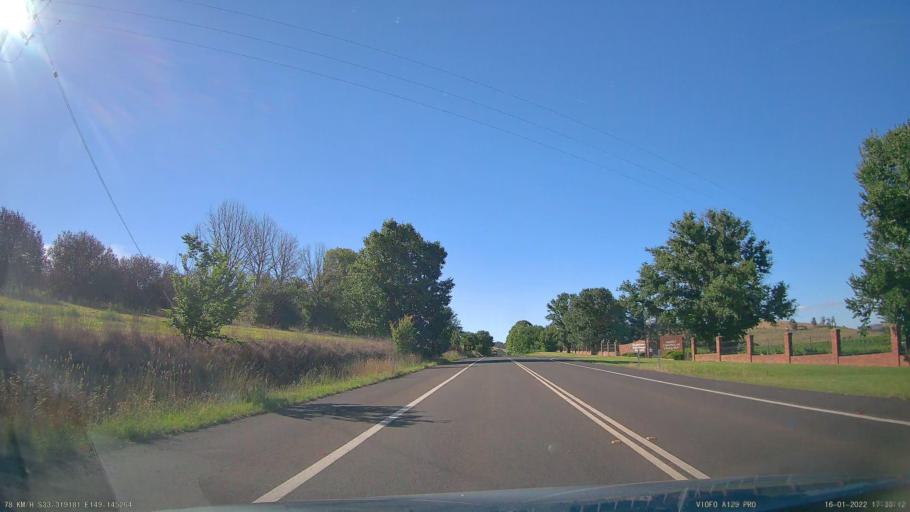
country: AU
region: New South Wales
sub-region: Orange Municipality
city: Orange
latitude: -33.3190
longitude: 149.1452
